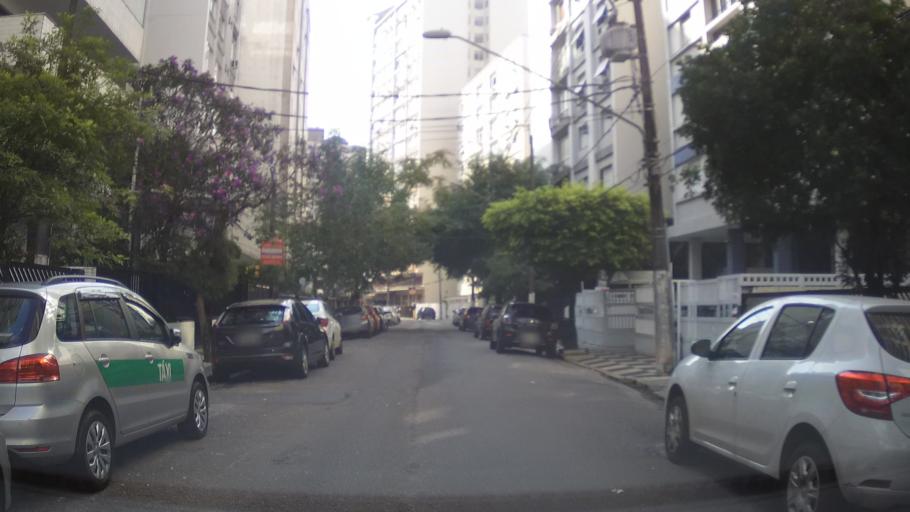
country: BR
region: Sao Paulo
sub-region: Santos
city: Santos
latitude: -23.9708
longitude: -46.3257
